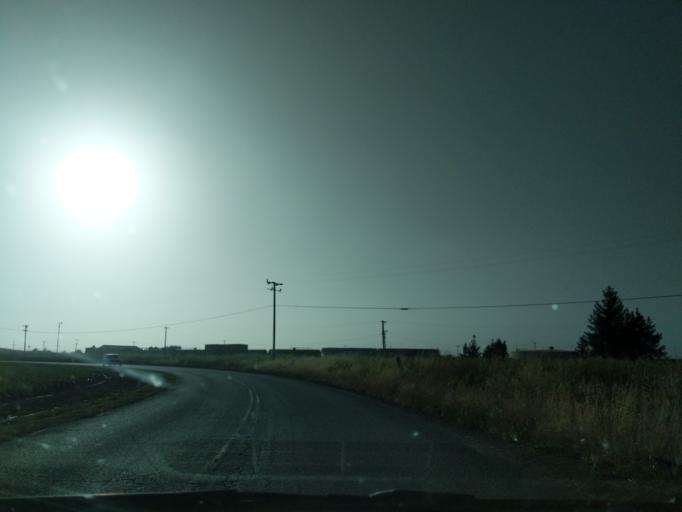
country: US
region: California
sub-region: Monterey County
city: Pajaro
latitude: 36.8963
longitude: -121.7362
